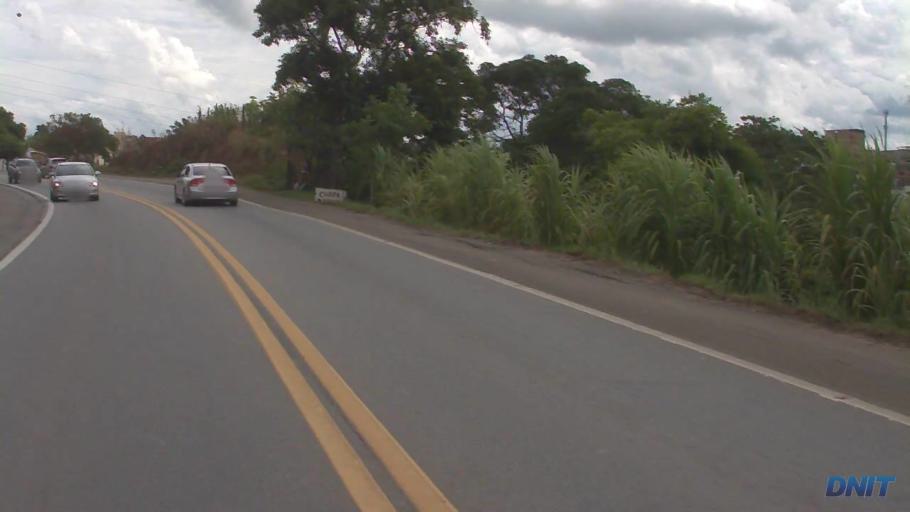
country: BR
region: Minas Gerais
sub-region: Ipatinga
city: Ipatinga
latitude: -19.4576
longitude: -42.5249
